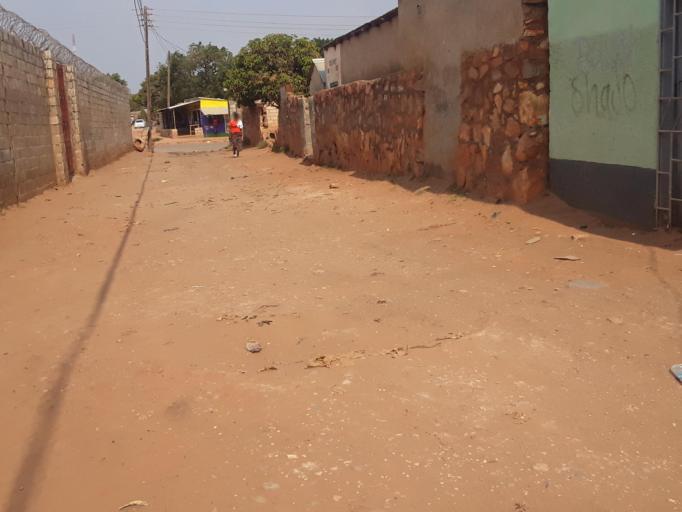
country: ZM
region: Lusaka
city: Lusaka
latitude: -15.3538
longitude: 28.3001
